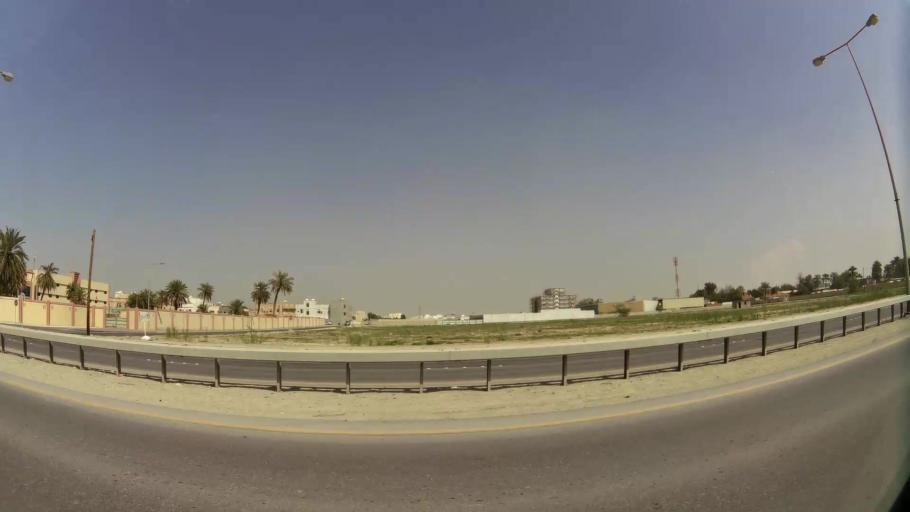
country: BH
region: Manama
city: Jidd Hafs
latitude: 26.2048
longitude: 50.4585
